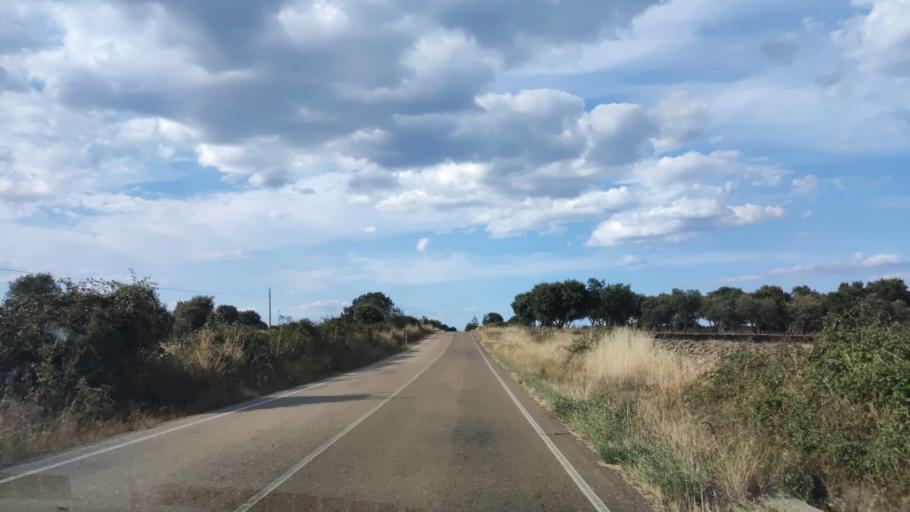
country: ES
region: Castille and Leon
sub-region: Provincia de Salamanca
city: Martiago
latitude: 40.4583
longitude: -6.4900
